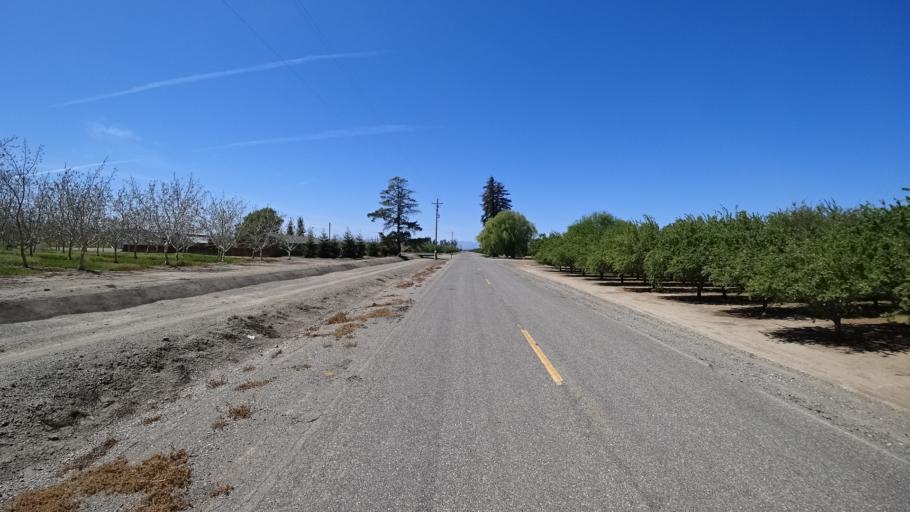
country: US
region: California
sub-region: Glenn County
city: Orland
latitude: 39.7249
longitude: -122.1118
